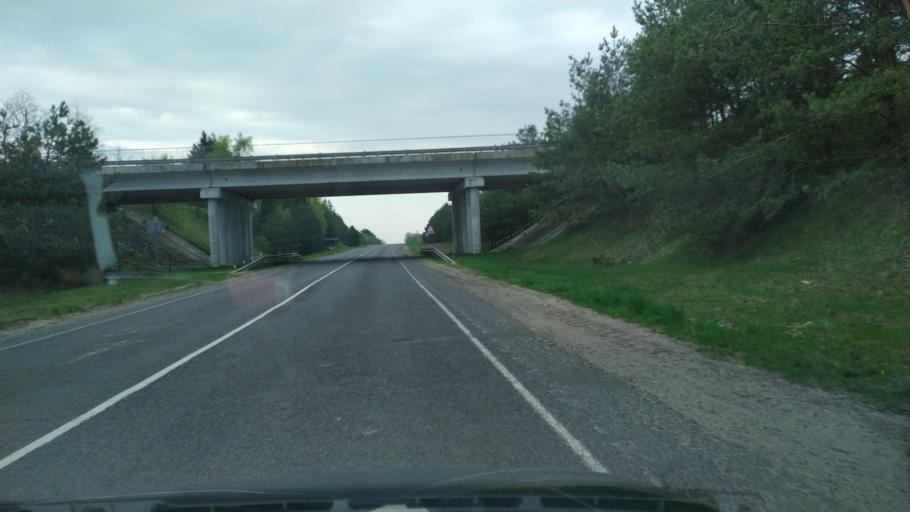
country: BY
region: Brest
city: Kamyanyets
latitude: 52.3427
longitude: 23.9060
